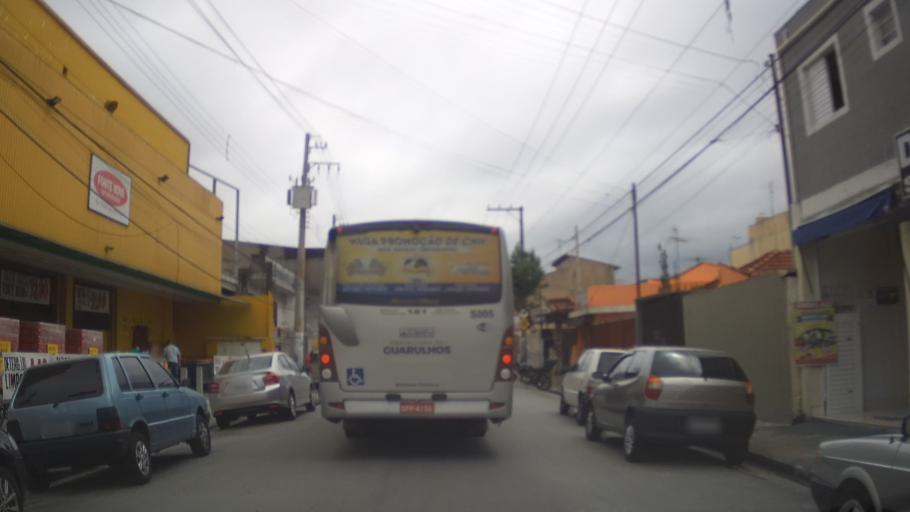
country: BR
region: Sao Paulo
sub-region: Guarulhos
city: Guarulhos
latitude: -23.4696
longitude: -46.5532
